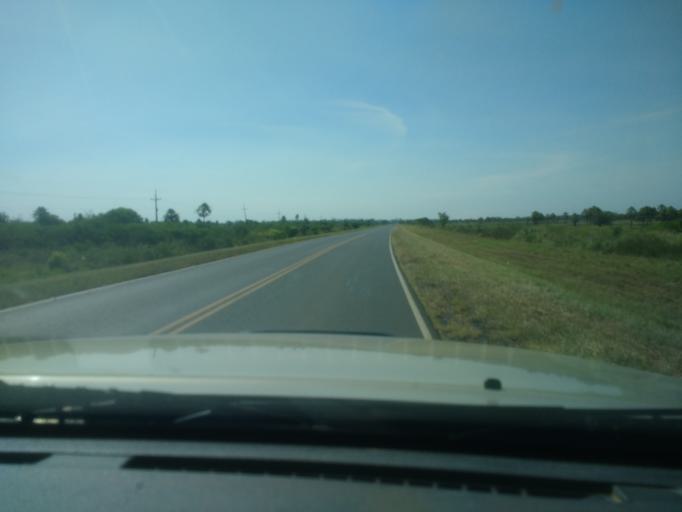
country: PY
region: Presidente Hayes
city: Benjamin Aceval
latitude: -24.9250
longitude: -57.5701
